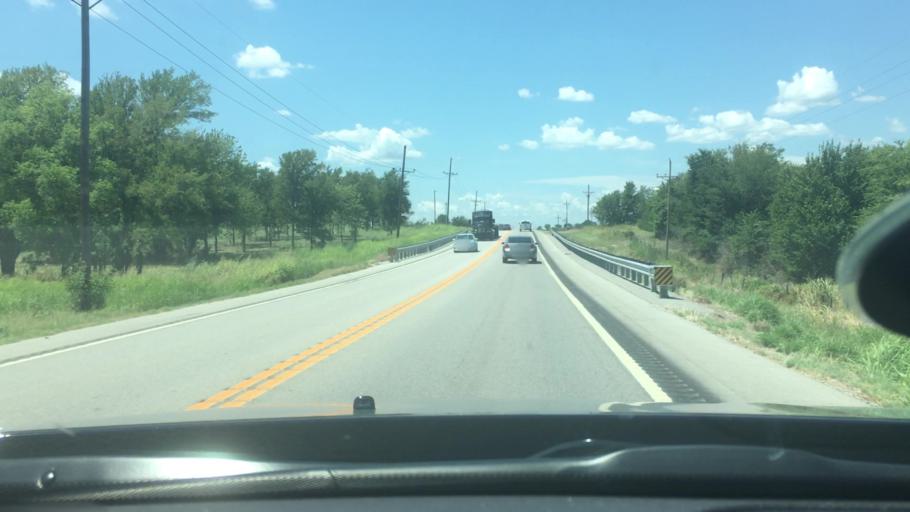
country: US
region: Oklahoma
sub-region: Bryan County
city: Durant
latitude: 33.9976
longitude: -96.2751
